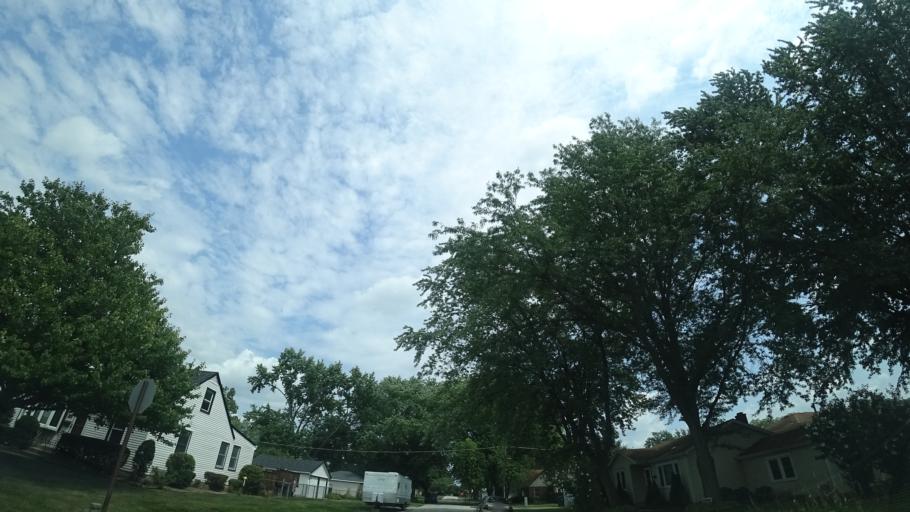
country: US
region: Illinois
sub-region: Cook County
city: Worth
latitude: 41.6867
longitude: -87.7843
